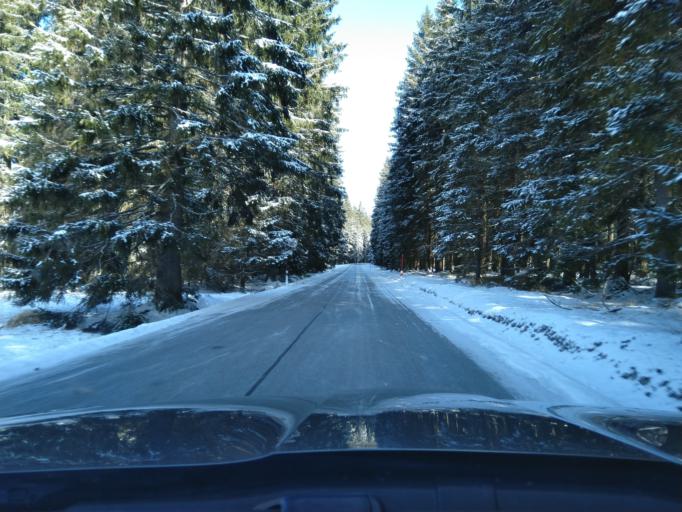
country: CZ
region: Jihocesky
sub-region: Okres Prachatice
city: Borova Lada
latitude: 49.0378
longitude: 13.5784
